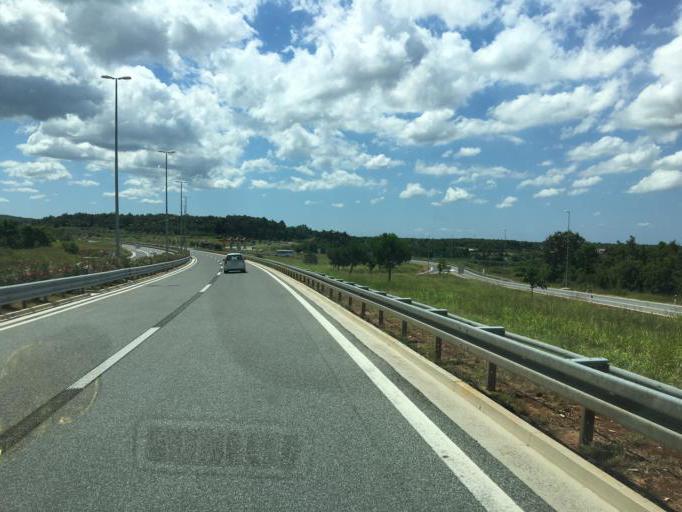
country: HR
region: Istarska
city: Karojba
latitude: 45.2778
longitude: 13.7082
